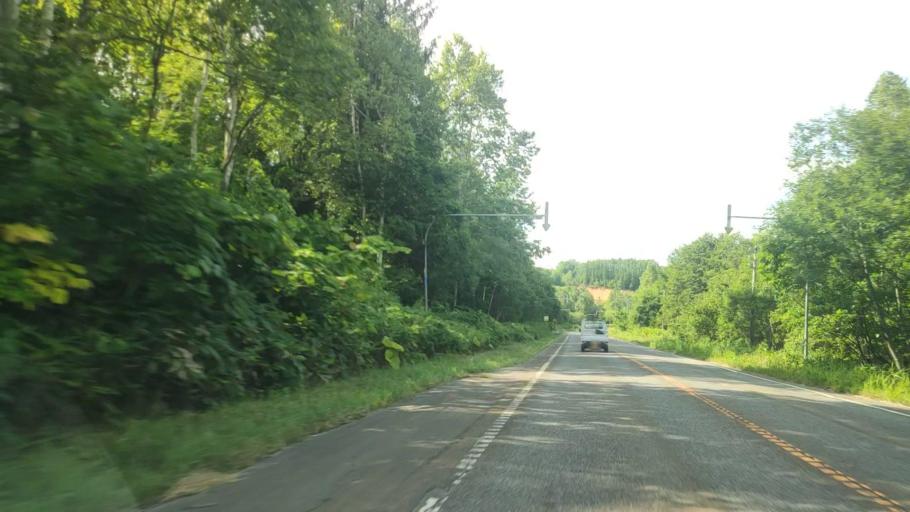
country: JP
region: Hokkaido
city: Nayoro
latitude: 44.3915
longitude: 142.3963
